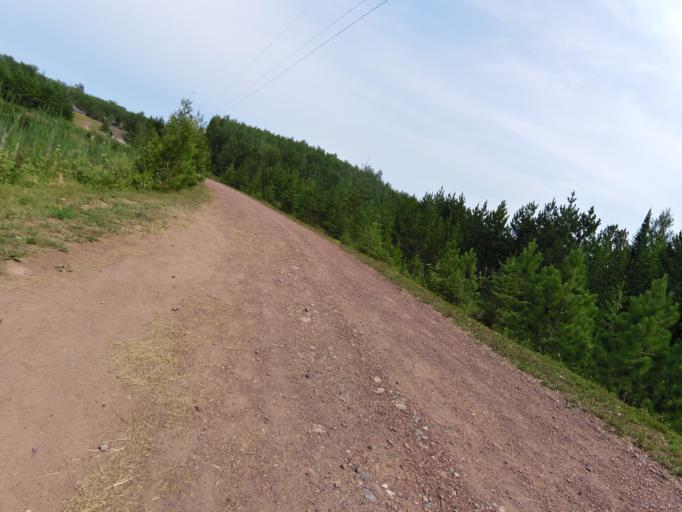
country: CA
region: Ontario
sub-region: Thunder Bay District
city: Thunder Bay
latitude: 48.7954
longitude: -88.6197
